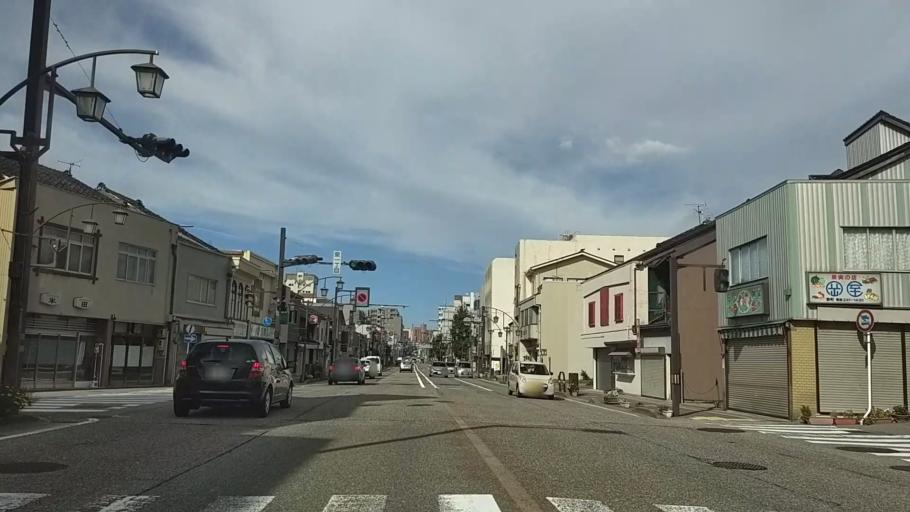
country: JP
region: Ishikawa
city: Nonoichi
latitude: 36.5516
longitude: 136.6452
